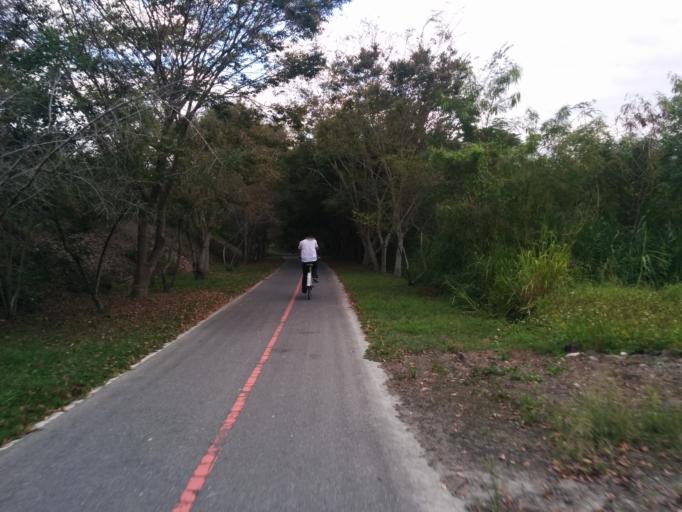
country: TW
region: Taiwan
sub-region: Taitung
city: Taitung
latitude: 23.0311
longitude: 121.1559
